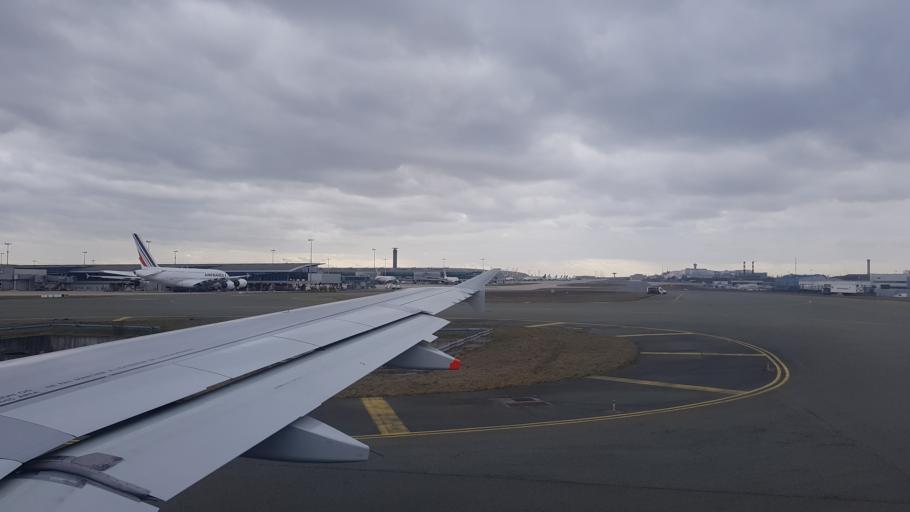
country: FR
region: Ile-de-France
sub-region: Departement de Seine-et-Marne
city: Mitry-Mory
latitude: 49.0098
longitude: 2.5952
